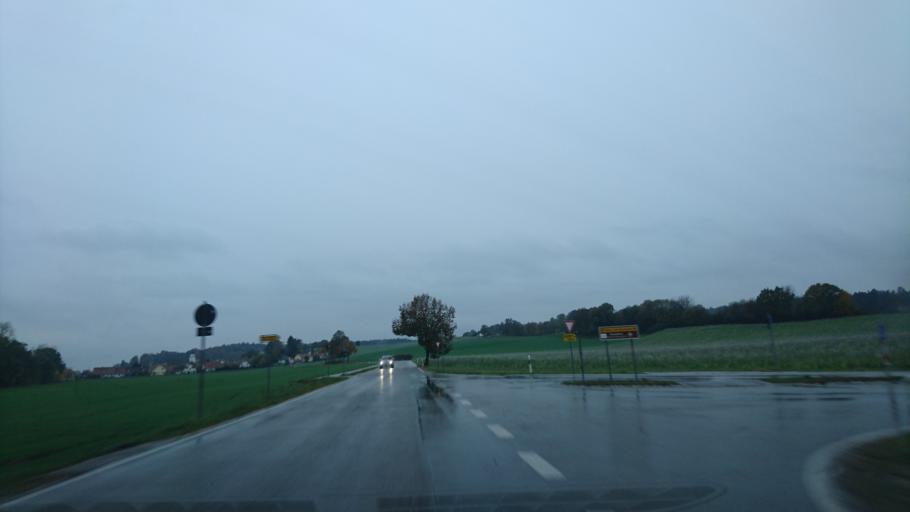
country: DE
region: Bavaria
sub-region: Swabia
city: Obergriesbach
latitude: 48.4348
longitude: 11.0950
